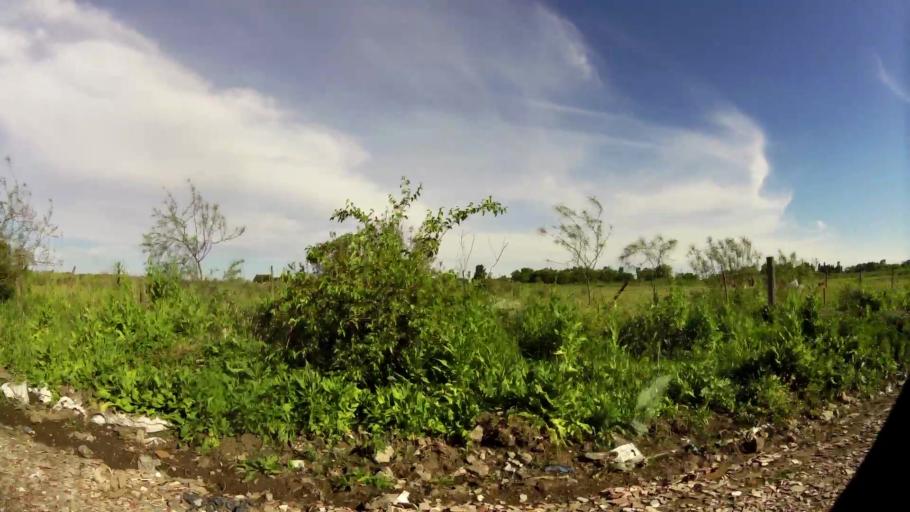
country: AR
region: Buenos Aires
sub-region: Partido de Almirante Brown
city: Adrogue
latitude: -34.8265
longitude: -58.3390
